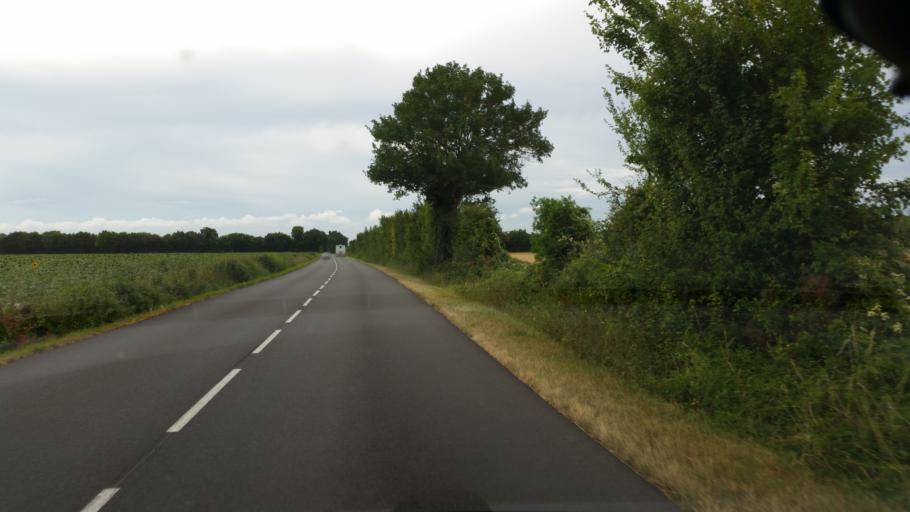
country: FR
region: Poitou-Charentes
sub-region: Departement de la Charente-Maritime
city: Surgeres
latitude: 46.1235
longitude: -0.7693
